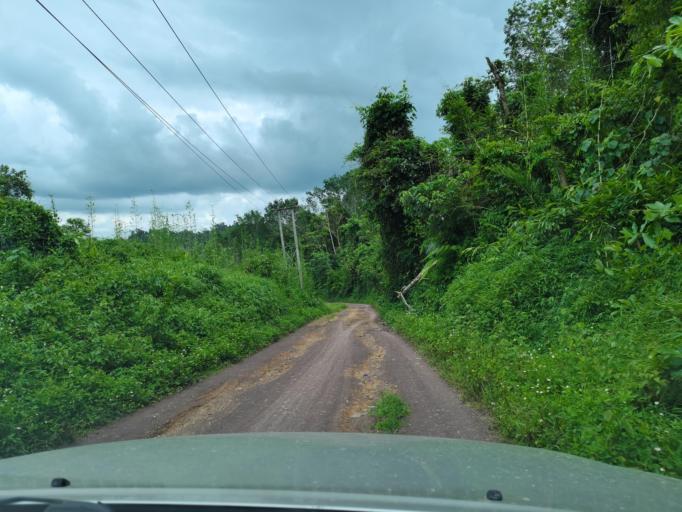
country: LA
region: Loungnamtha
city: Muang Long
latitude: 20.7028
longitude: 101.0144
